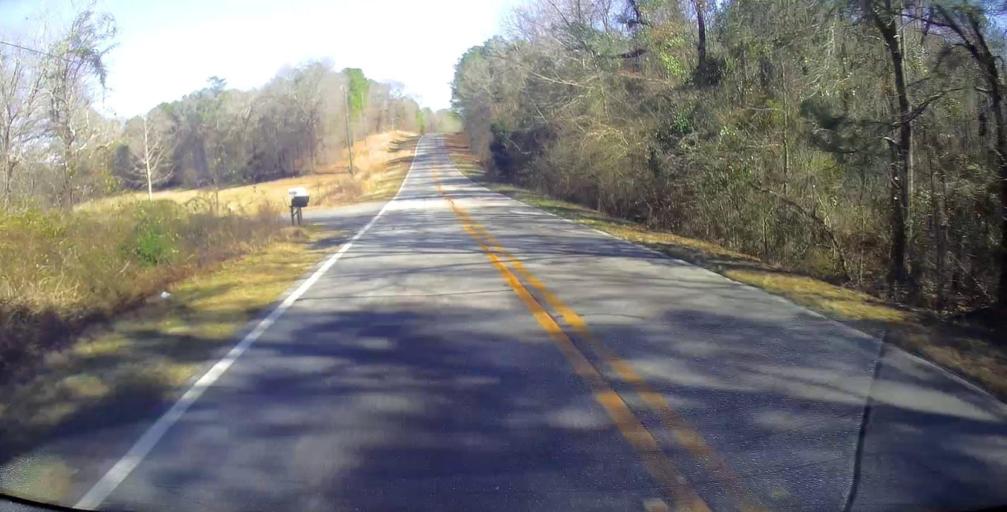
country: US
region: Georgia
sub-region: Peach County
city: Byron
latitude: 32.6111
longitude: -83.8137
